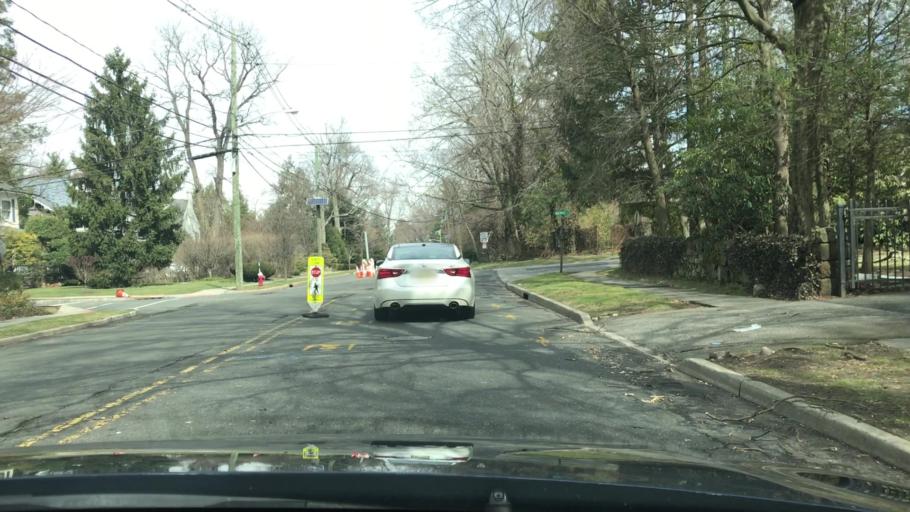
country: US
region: New Jersey
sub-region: Bergen County
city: Englewood
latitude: 40.8928
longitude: -73.9667
